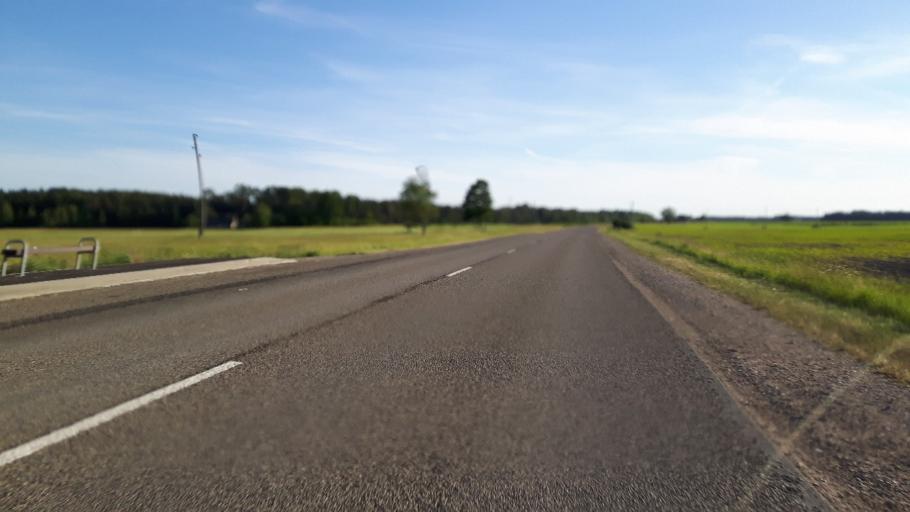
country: LV
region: Kuldigas Rajons
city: Kuldiga
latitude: 57.0293
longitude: 22.1951
